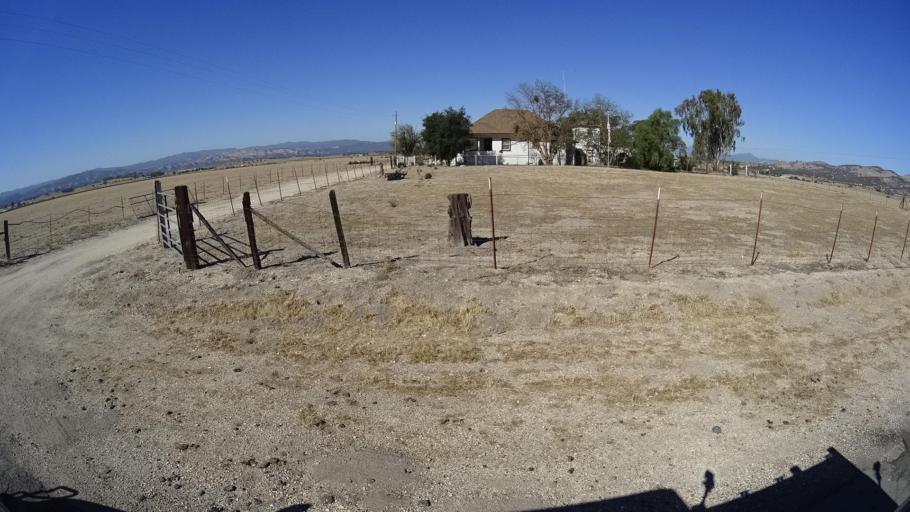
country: US
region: California
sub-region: Monterey County
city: King City
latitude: 35.9684
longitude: -121.0850
